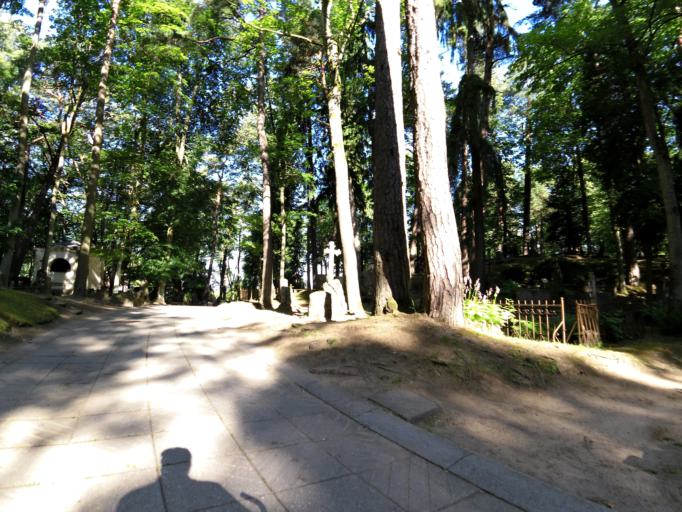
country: LT
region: Vilnius County
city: Rasos
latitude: 54.6986
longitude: 25.3195
